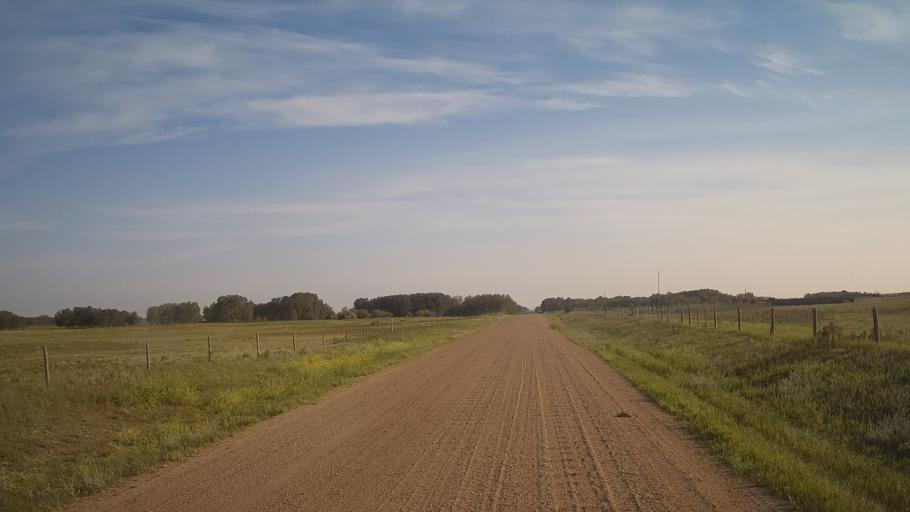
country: CA
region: Saskatchewan
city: Saskatoon
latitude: 51.8258
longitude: -106.5239
